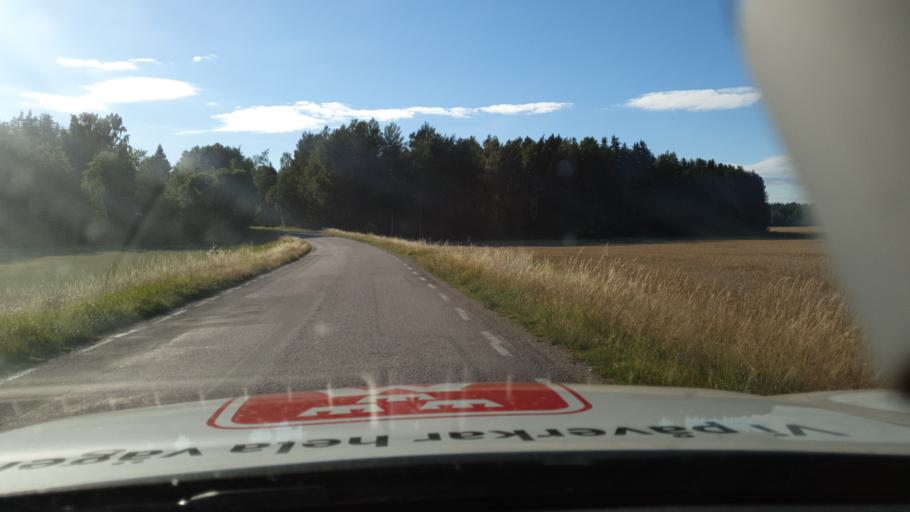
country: SE
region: Vaestra Goetaland
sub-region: Toreboda Kommun
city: Toereboda
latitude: 58.8193
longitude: 14.0267
